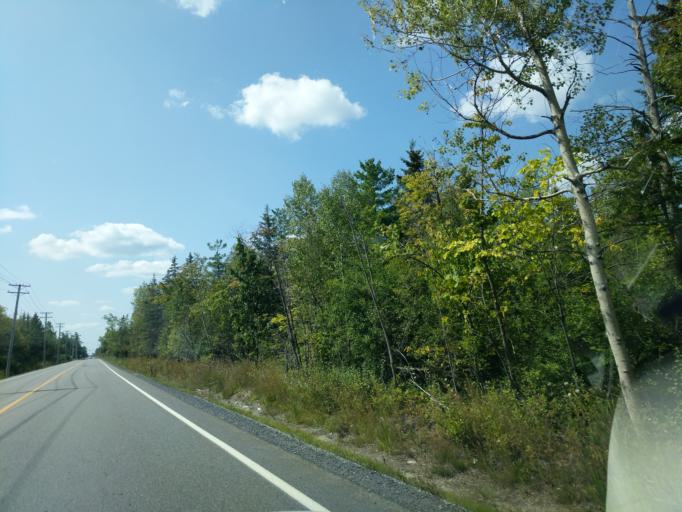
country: CA
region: Ontario
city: Bells Corners
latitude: 45.4397
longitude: -75.8487
